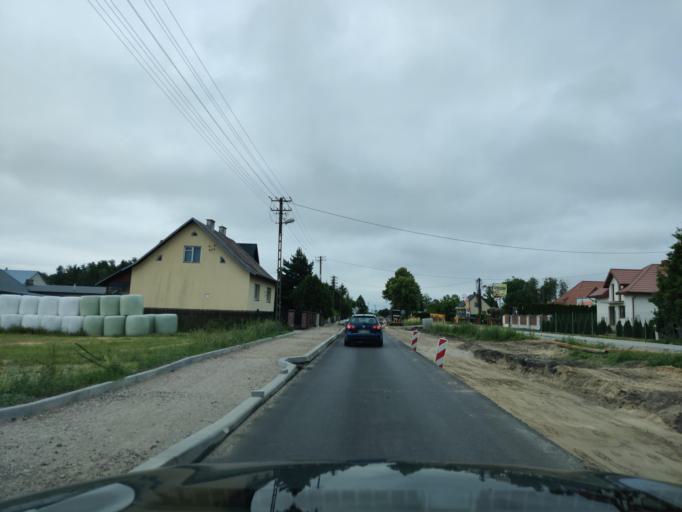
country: PL
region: Warmian-Masurian Voivodeship
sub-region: Powiat szczycienski
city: Rozogi
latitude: 53.4774
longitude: 21.3659
